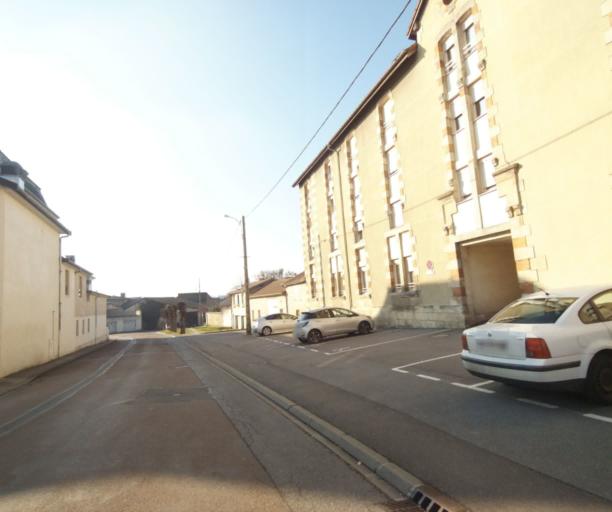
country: FR
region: Champagne-Ardenne
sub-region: Departement de la Haute-Marne
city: Wassy
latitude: 48.4992
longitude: 4.9507
